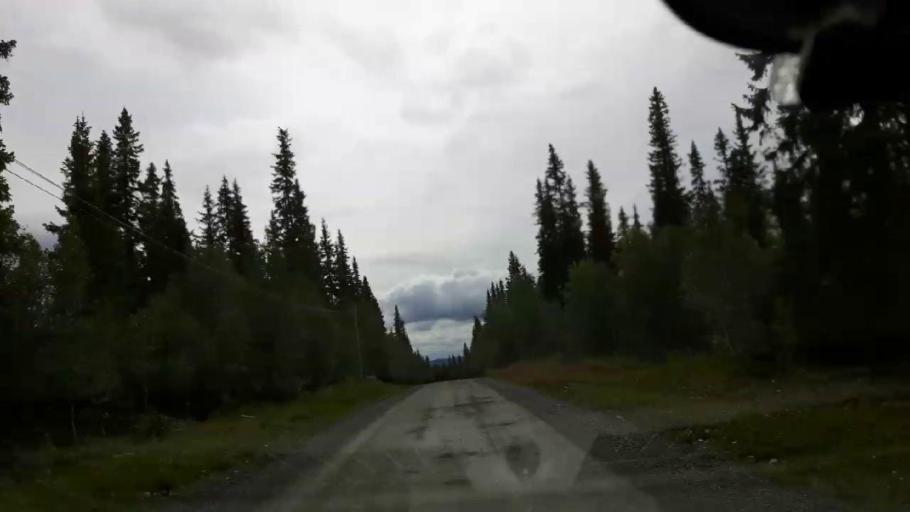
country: SE
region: Jaemtland
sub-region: Krokoms Kommun
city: Valla
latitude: 63.7166
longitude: 13.8592
